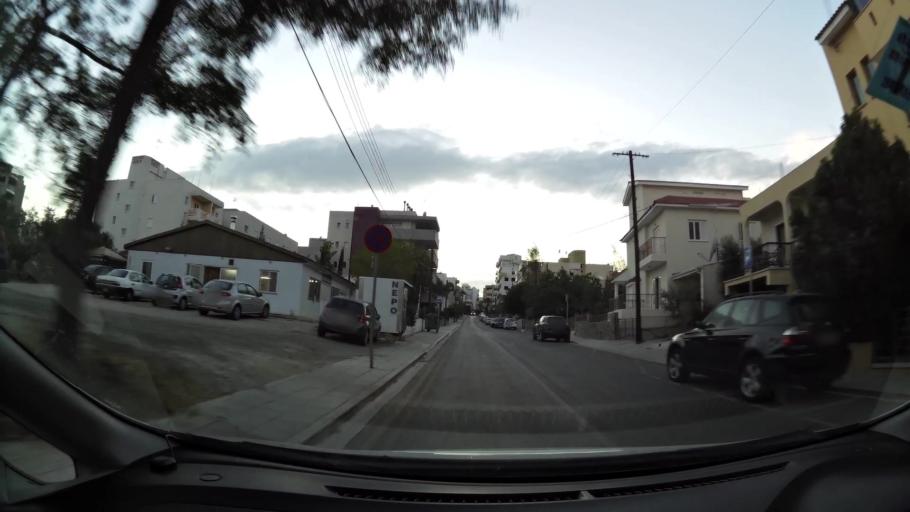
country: CY
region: Lefkosia
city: Nicosia
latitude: 35.1654
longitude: 33.3771
